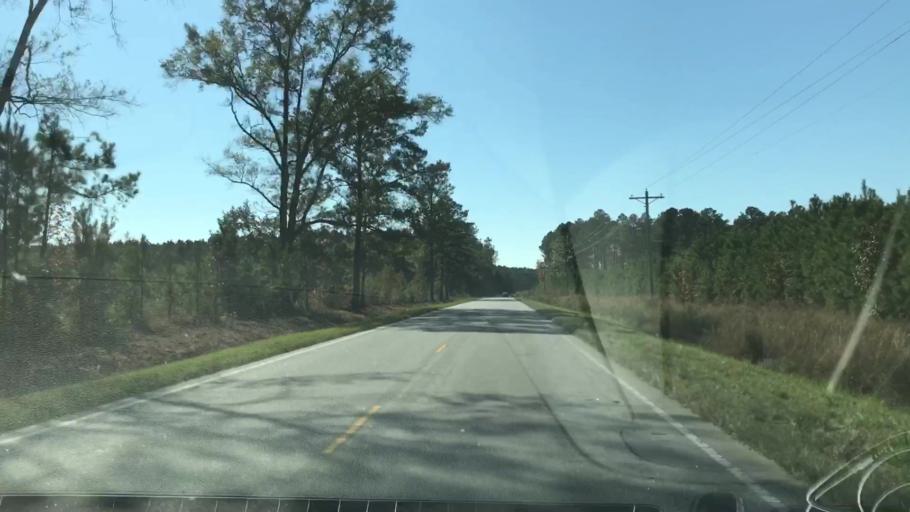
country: US
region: South Carolina
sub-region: Jasper County
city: Ridgeland
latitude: 32.4196
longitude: -80.8988
